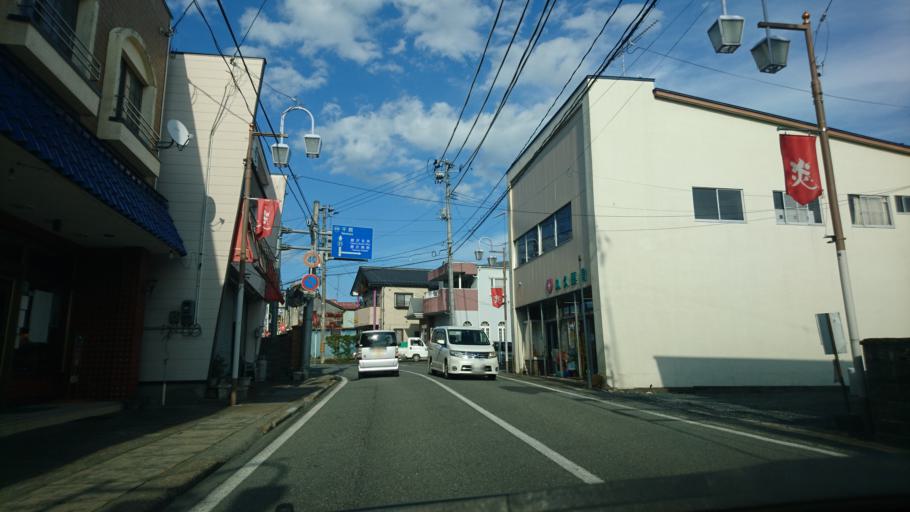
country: JP
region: Iwate
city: Ichinoseki
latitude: 38.8614
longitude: 141.3479
